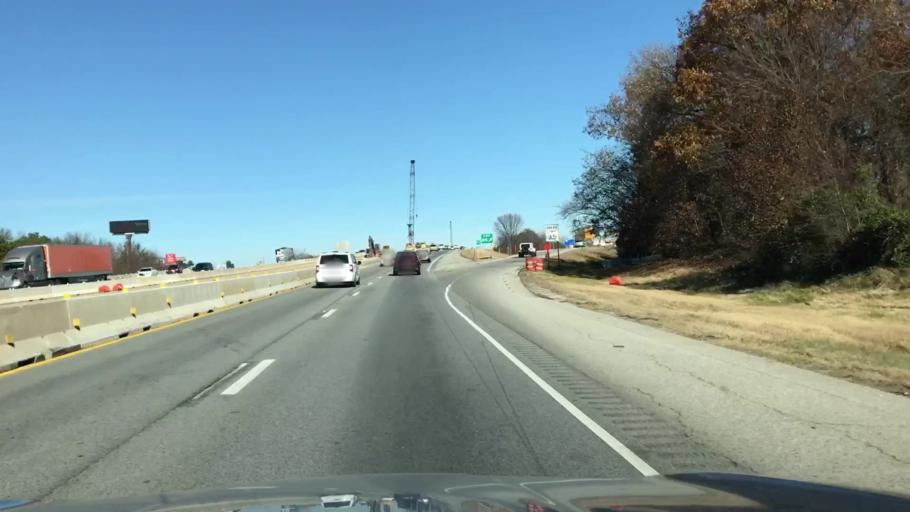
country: US
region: Arkansas
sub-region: Benton County
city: Bentonville
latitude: 36.3313
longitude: -94.1843
